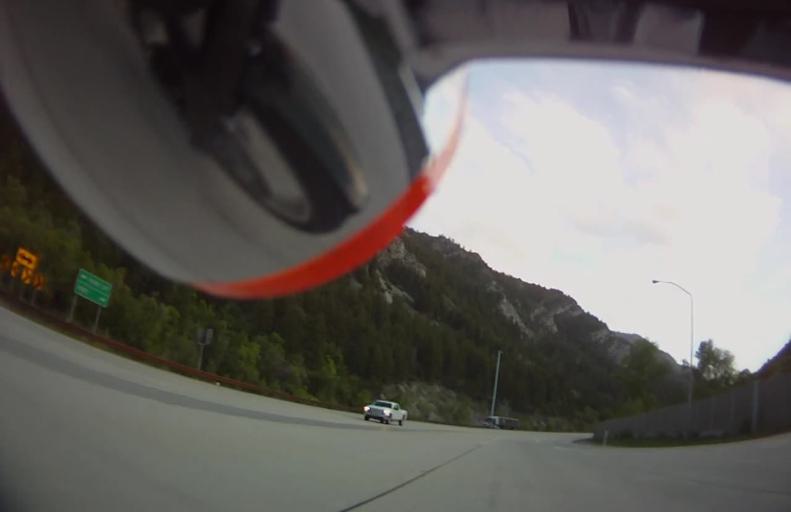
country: US
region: Utah
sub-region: Utah County
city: Orem
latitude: 40.3658
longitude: -111.5557
